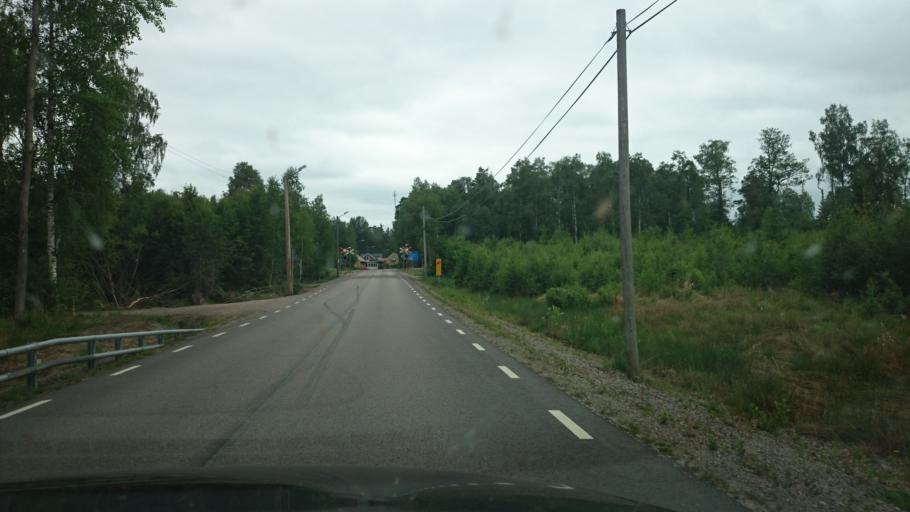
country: SE
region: Halland
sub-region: Hylte Kommun
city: Torup
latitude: 56.9635
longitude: 13.1486
